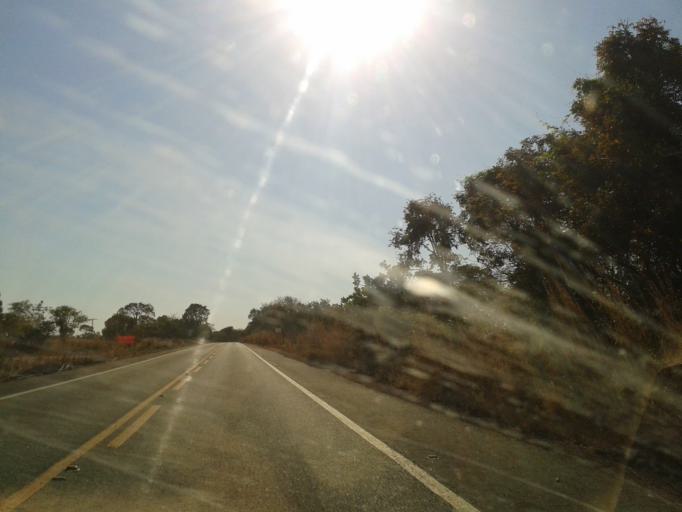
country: BR
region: Goias
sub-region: Mozarlandia
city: Mozarlandia
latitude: -14.9310
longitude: -50.5579
